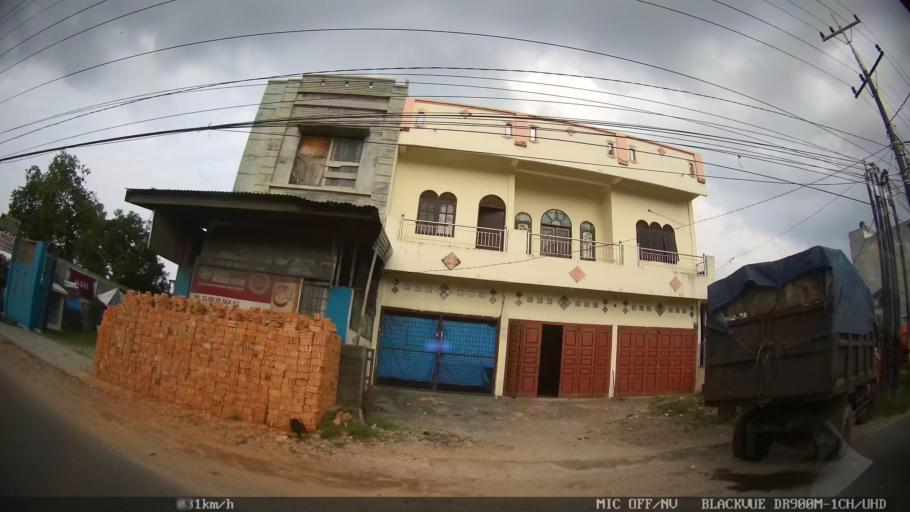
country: ID
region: North Sumatra
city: Sunggal
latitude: 3.5302
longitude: 98.6200
